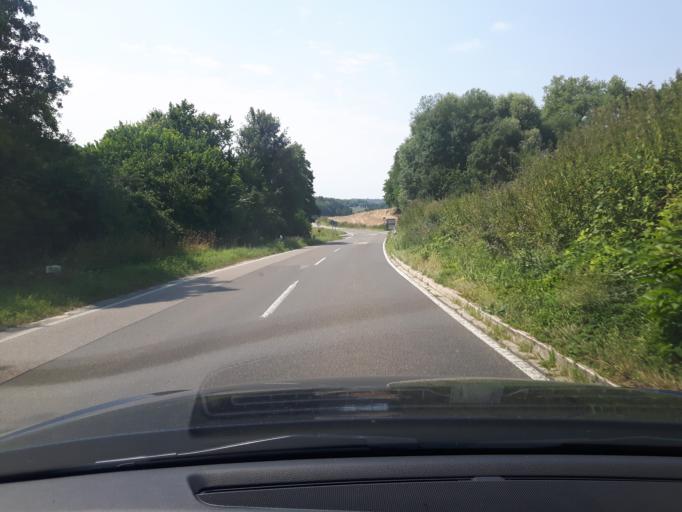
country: DE
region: Baden-Wuerttemberg
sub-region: Karlsruhe Region
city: Zaisenhausen
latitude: 49.1803
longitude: 8.8105
